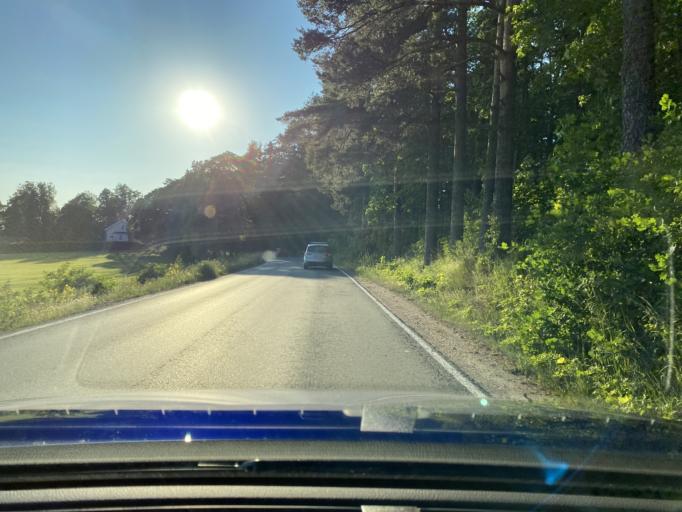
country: FI
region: Haeme
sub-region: Haemeenlinna
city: Tervakoski
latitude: 60.7397
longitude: 24.6587
